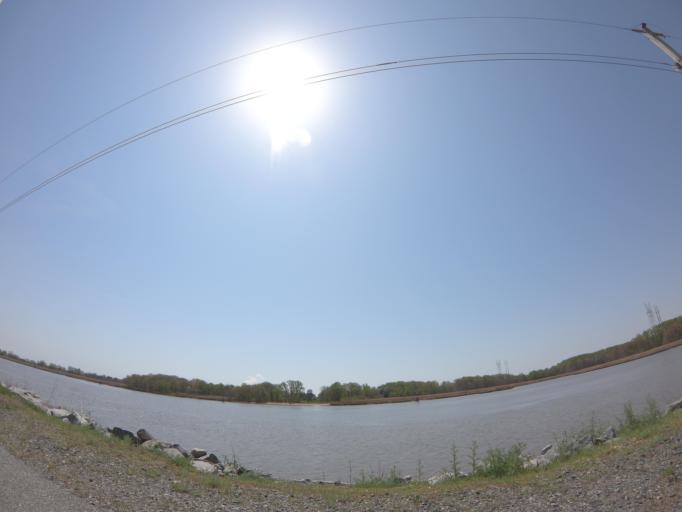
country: US
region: Delaware
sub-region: New Castle County
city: Delaware City
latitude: 39.5559
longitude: -75.6178
